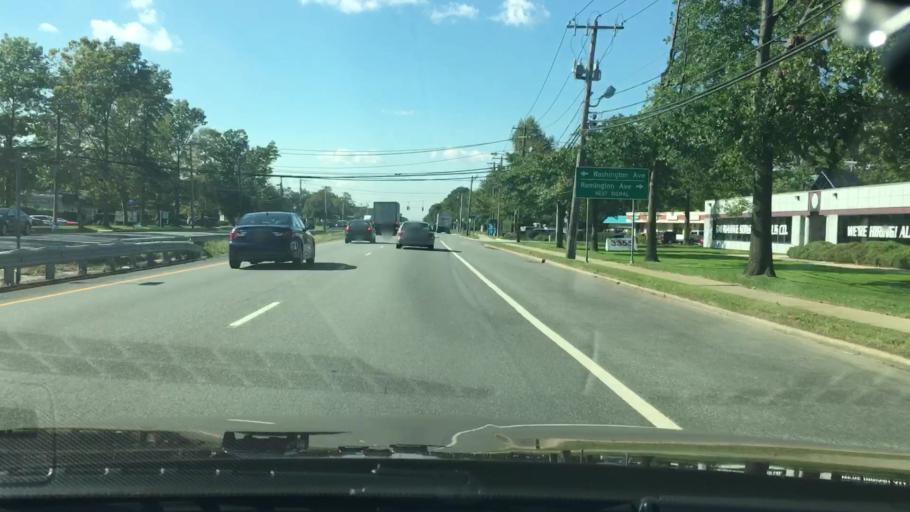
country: US
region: New York
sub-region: Suffolk County
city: Bohemia
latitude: 40.7874
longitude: -73.1277
